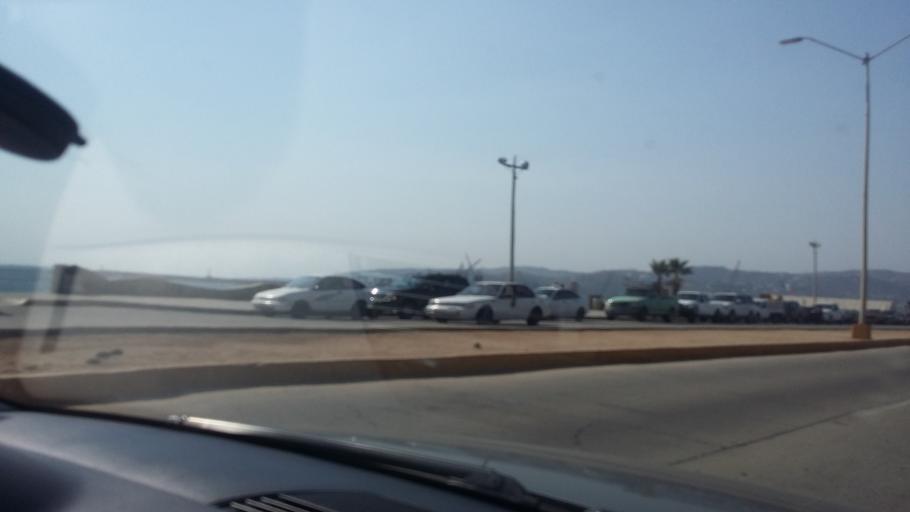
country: MX
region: Baja California
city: Ensenada
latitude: 31.8384
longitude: -116.6104
